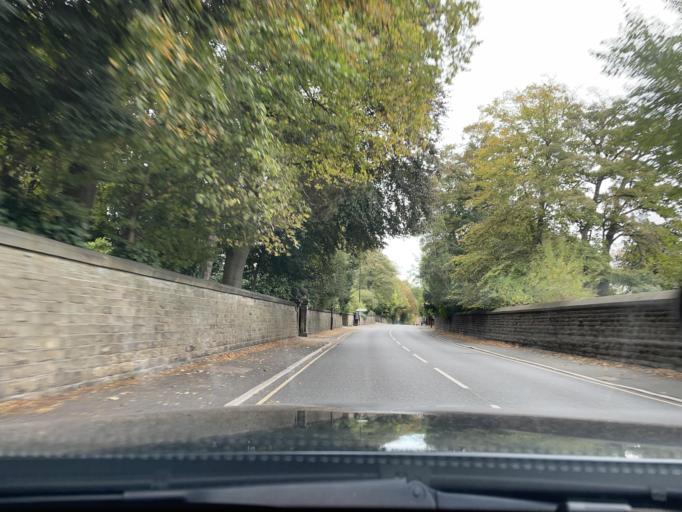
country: GB
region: England
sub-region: Sheffield
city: Sheffield
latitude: 53.3767
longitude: -1.5109
